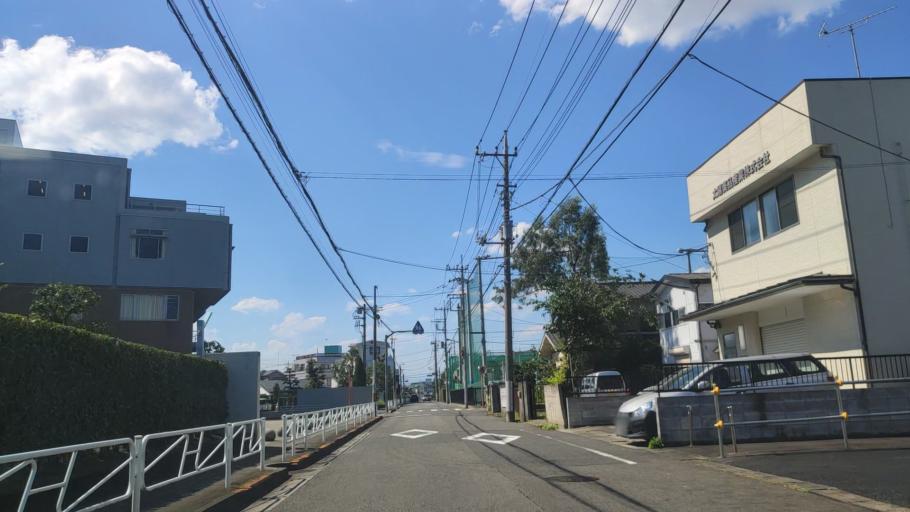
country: JP
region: Tokyo
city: Hachioji
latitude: 35.6513
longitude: 139.3296
